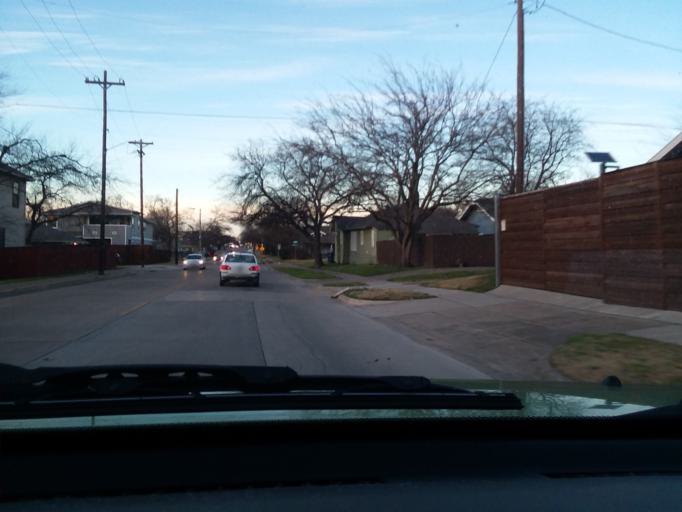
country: US
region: Texas
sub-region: Dallas County
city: Highland Park
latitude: 32.8202
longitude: -96.7702
